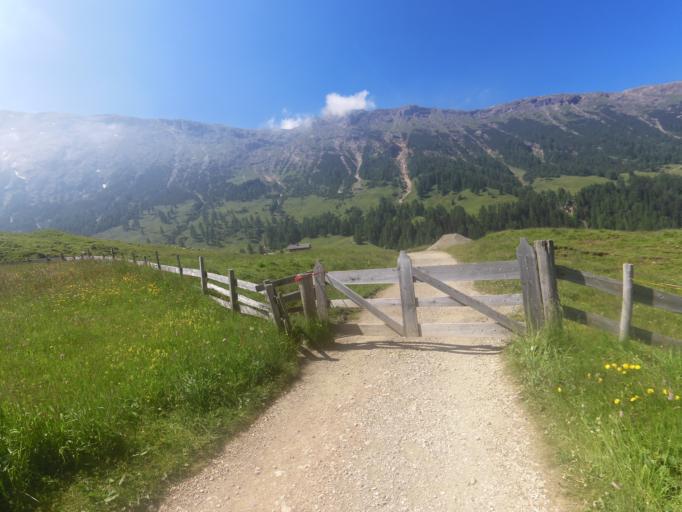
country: IT
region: Trentino-Alto Adige
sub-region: Bolzano
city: Siusi
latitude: 46.5157
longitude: 11.6081
